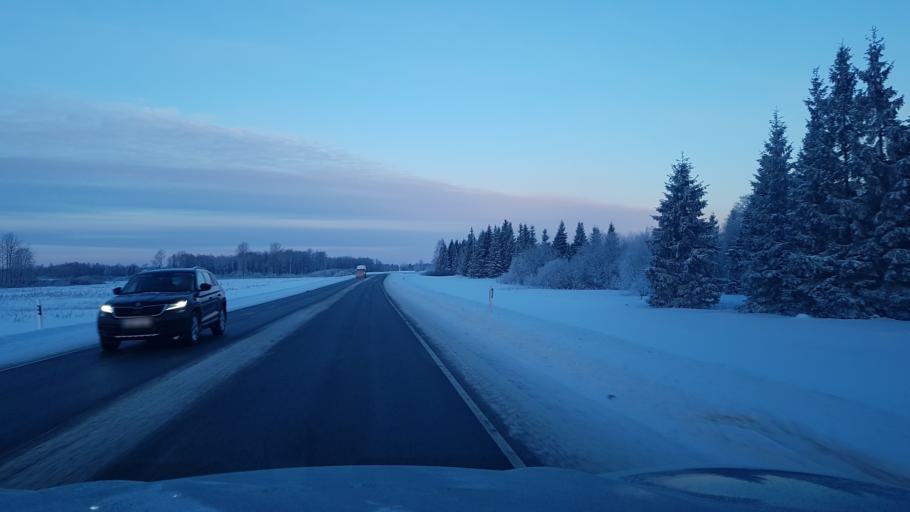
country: EE
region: Ida-Virumaa
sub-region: Narva-Joesuu linn
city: Narva-Joesuu
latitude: 59.3925
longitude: 28.0886
